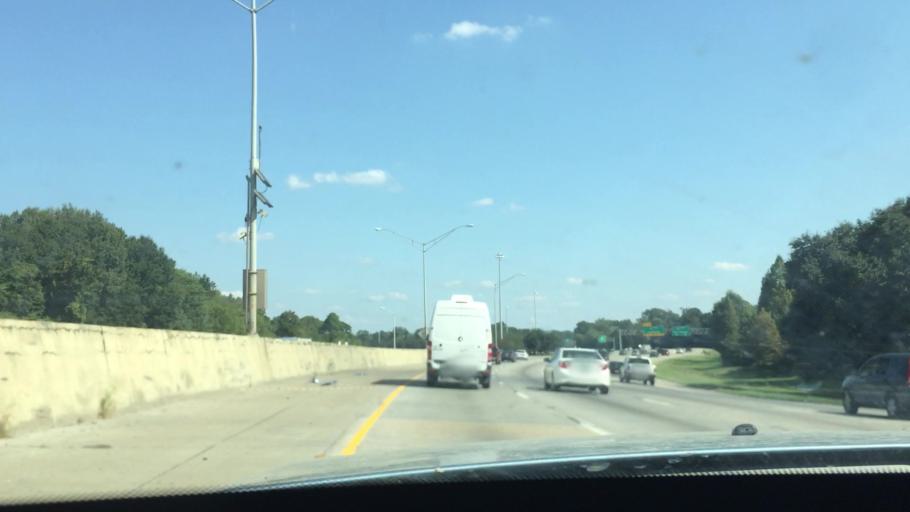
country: US
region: Louisiana
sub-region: East Baton Rouge Parish
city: Westminster
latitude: 30.4208
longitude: -91.1235
